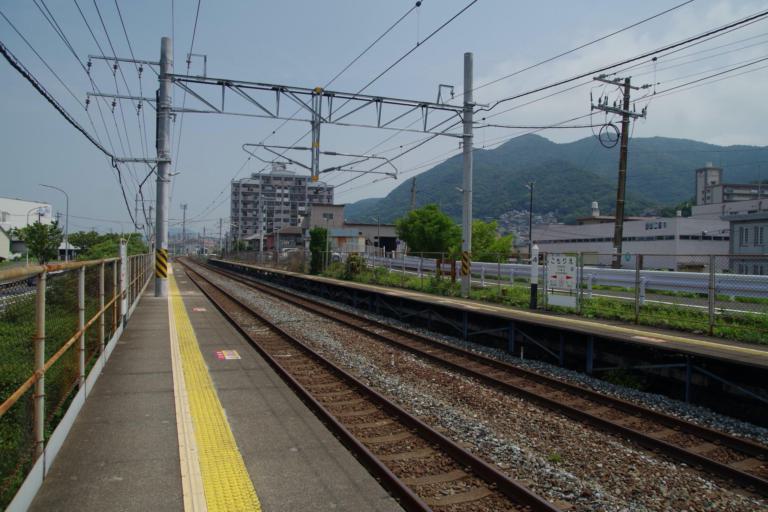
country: JP
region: Yamaguchi
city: Shimonoseki
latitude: 33.9162
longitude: 130.9387
